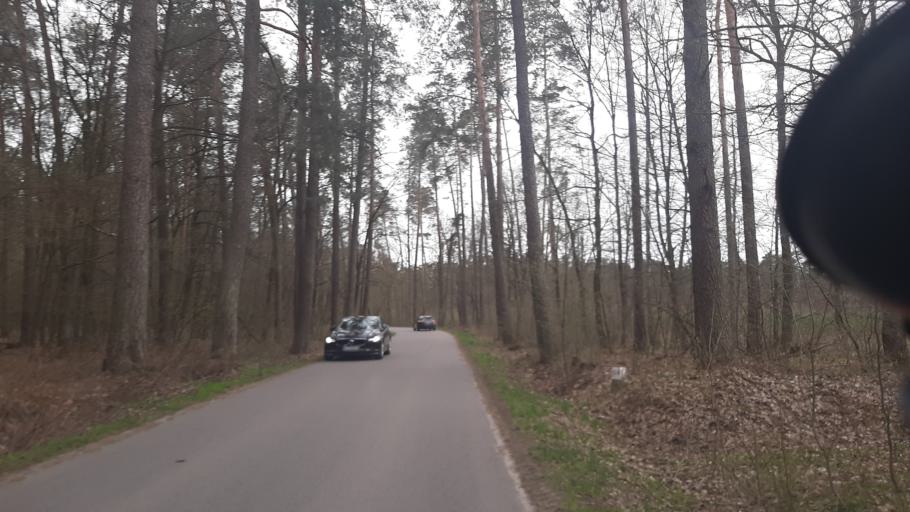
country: PL
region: Lublin Voivodeship
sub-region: Powiat lubelski
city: Niemce
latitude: 51.3769
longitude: 22.5533
